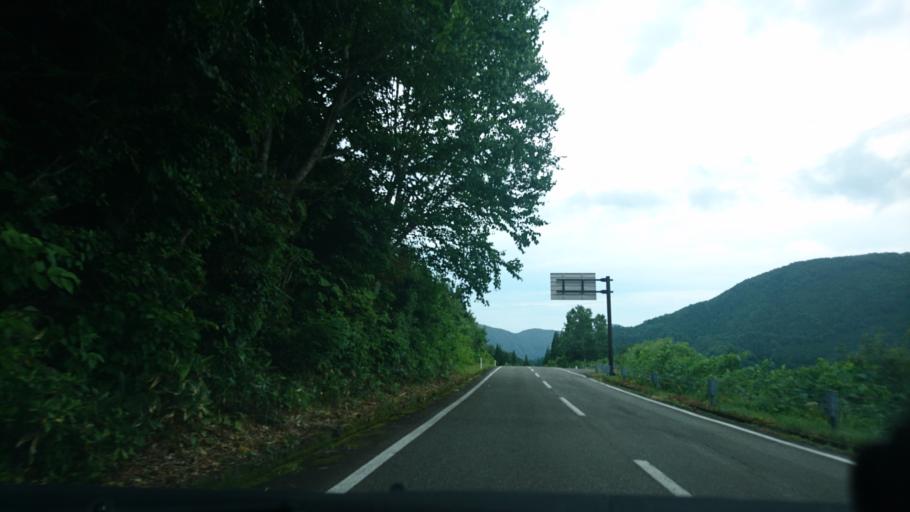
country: JP
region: Akita
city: Yuzawa
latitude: 39.1589
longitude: 140.7492
